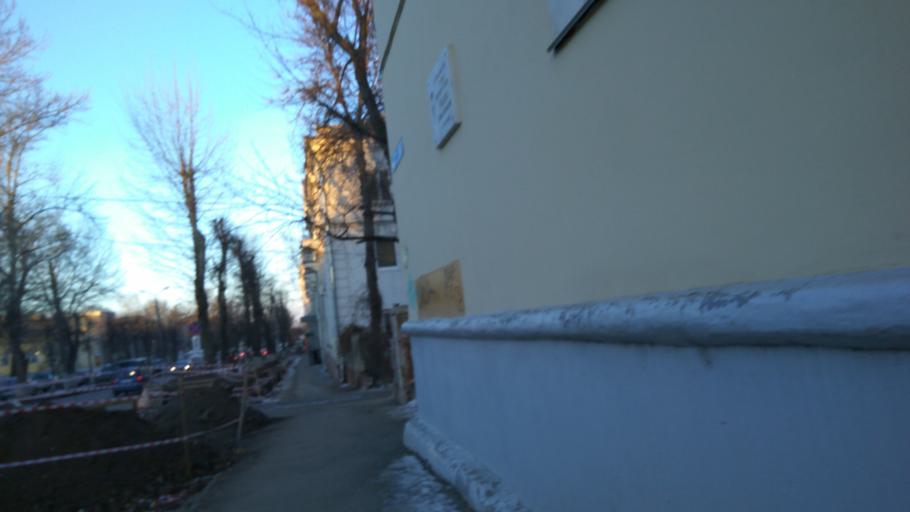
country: RU
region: Tula
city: Tula
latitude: 54.1803
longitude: 37.5997
